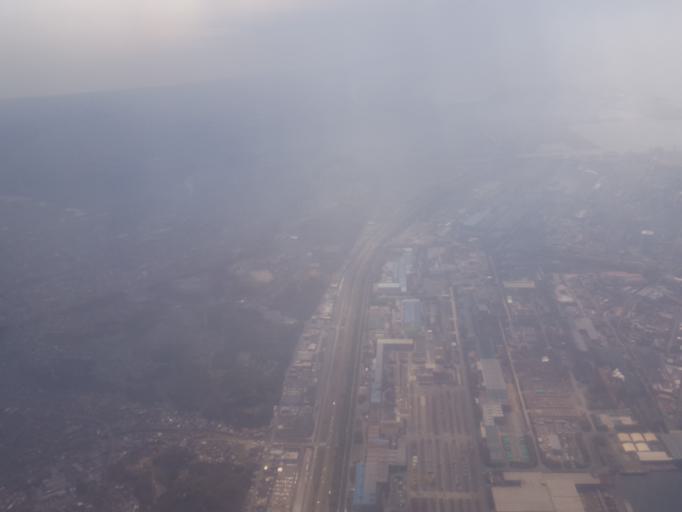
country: JP
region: Chiba
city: Kisarazu
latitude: 35.3579
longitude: 139.9122
